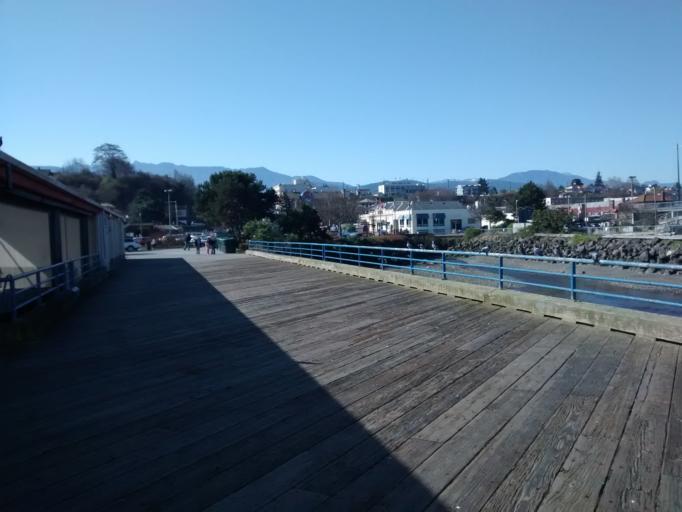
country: US
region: Washington
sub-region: Clallam County
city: Port Angeles
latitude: 48.1208
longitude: -123.4287
